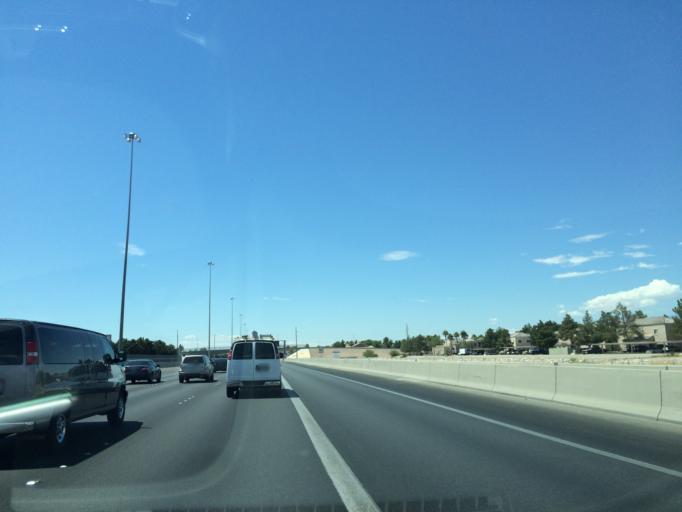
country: US
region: Nevada
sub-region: Clark County
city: Las Vegas
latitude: 36.2364
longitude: -115.2471
